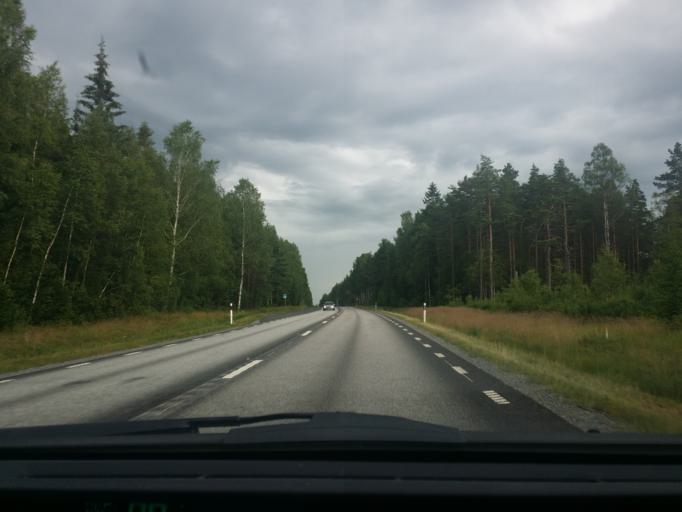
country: SE
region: OErebro
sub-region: Nora Kommun
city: Nora
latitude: 59.4861
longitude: 15.0683
